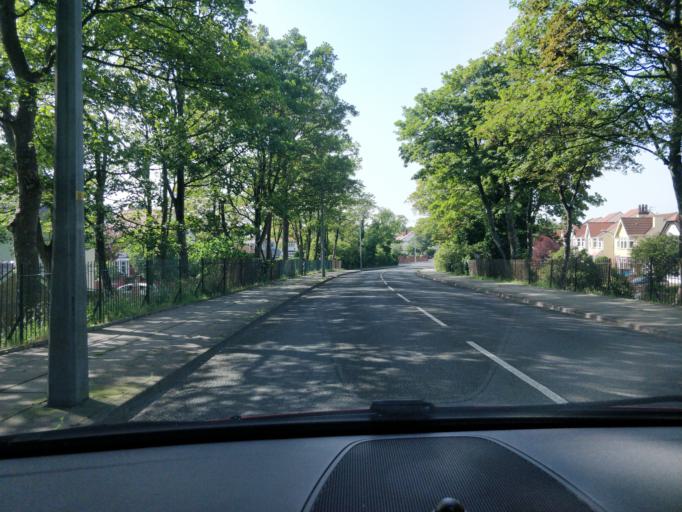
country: GB
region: England
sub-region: Sefton
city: Southport
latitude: 53.6573
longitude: -2.9764
